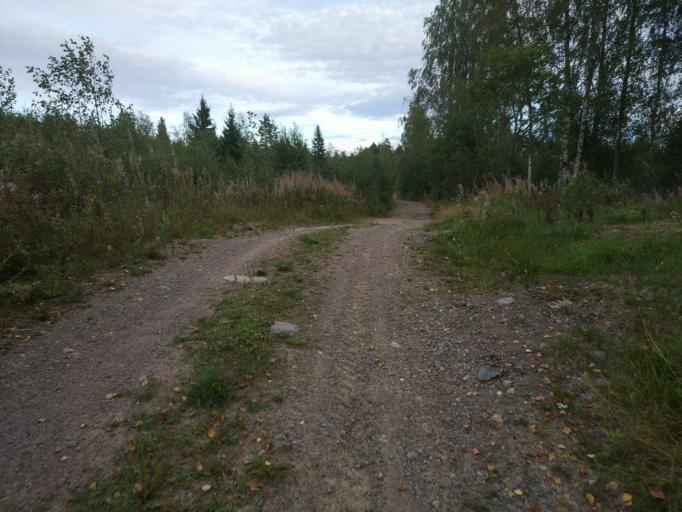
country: RU
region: Leningrad
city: Kuznechnoye
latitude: 61.1176
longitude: 29.6011
